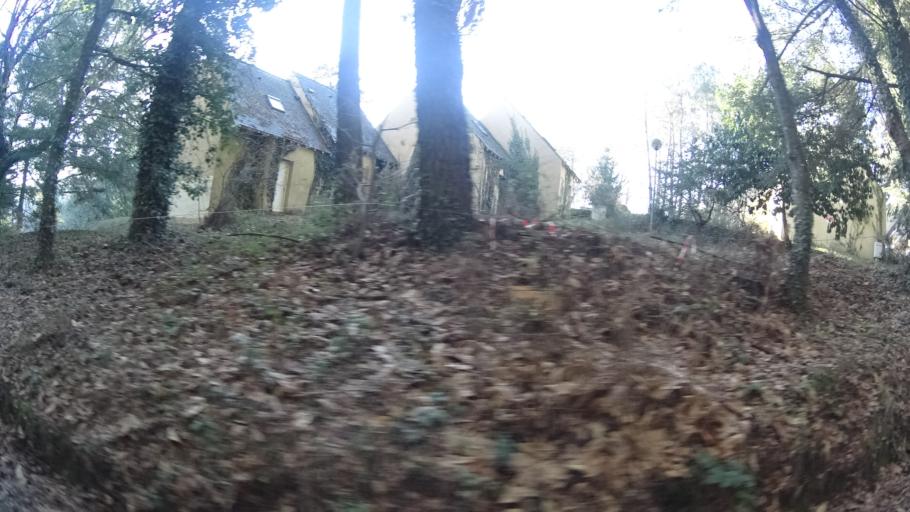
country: FR
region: Brittany
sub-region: Departement du Morbihan
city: Saint-Jacut-les-Pins
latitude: 47.6649
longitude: -2.1890
